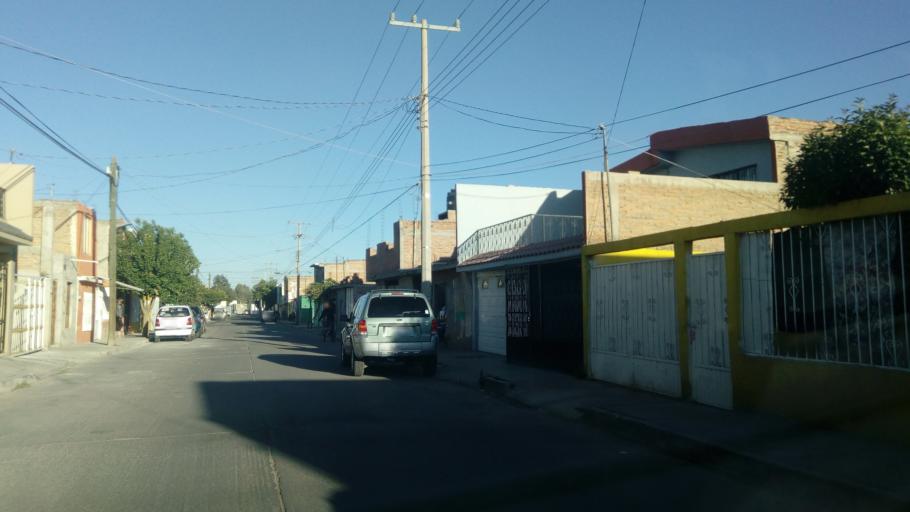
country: MX
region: Durango
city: Victoria de Durango
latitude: 23.9978
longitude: -104.6814
